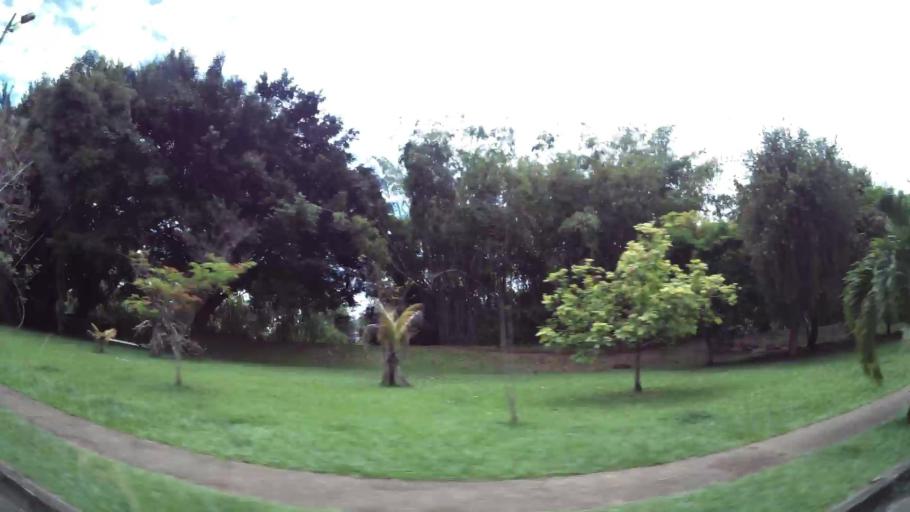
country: CO
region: Valle del Cauca
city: Cali
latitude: 3.3857
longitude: -76.5344
